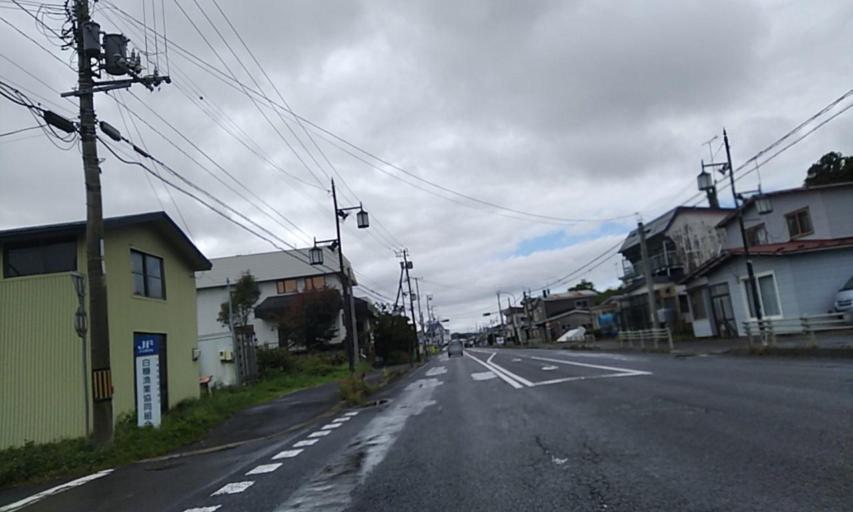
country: JP
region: Hokkaido
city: Kushiro
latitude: 42.9535
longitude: 144.0869
